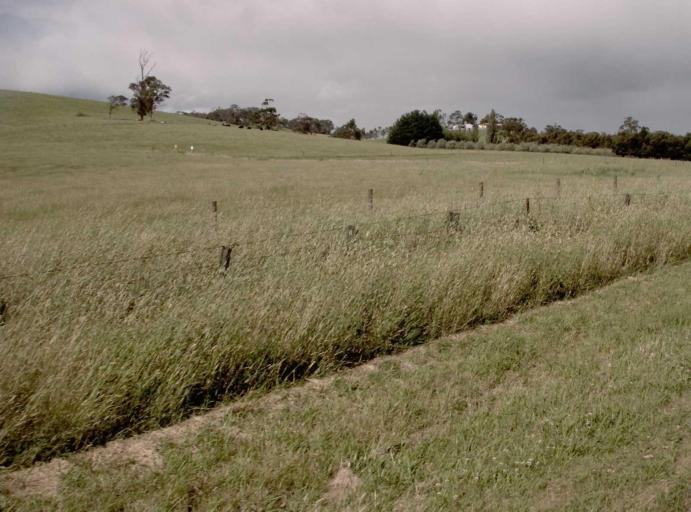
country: AU
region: Victoria
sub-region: Latrobe
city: Traralgon
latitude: -38.1502
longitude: 146.4638
